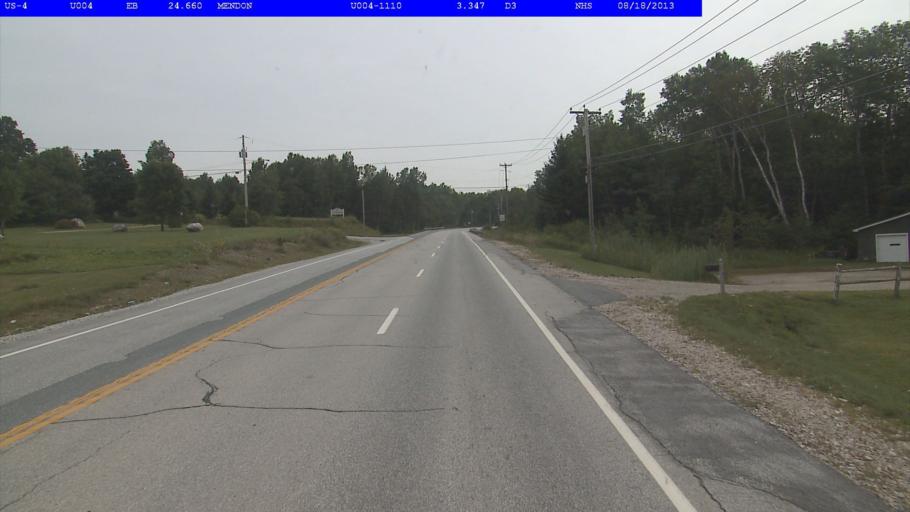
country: US
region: Vermont
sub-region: Rutland County
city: Rutland
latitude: 43.6536
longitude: -72.8900
